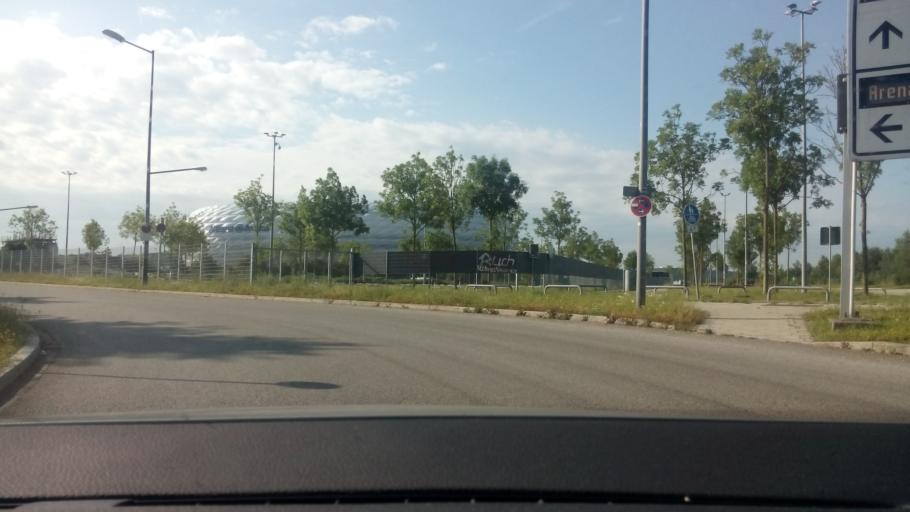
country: DE
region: Bavaria
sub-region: Upper Bavaria
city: Unterfoehring
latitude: 48.2235
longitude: 11.6211
